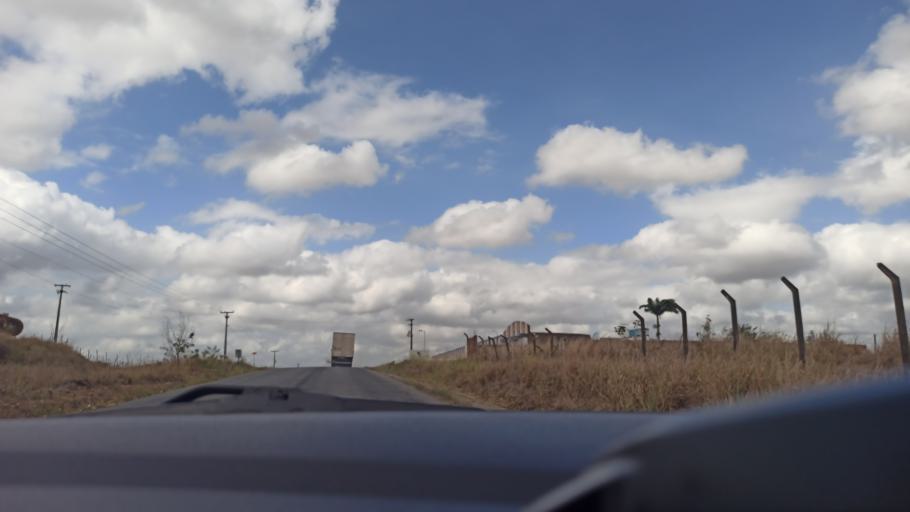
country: BR
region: Pernambuco
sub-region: Timbauba
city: Timbauba
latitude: -7.4783
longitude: -35.2834
